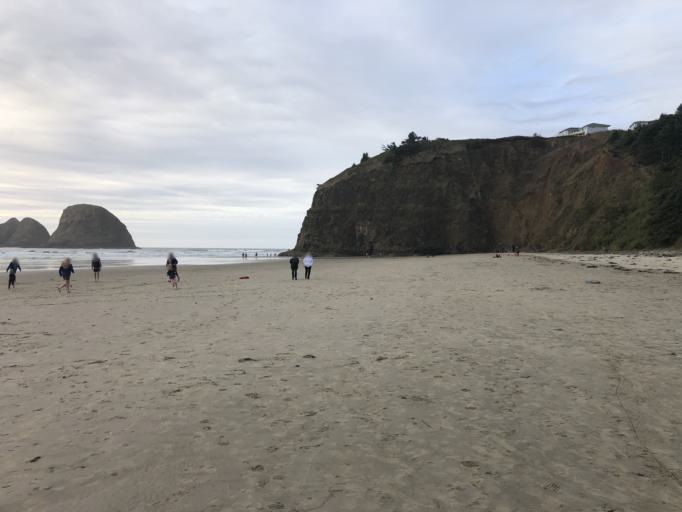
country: US
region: Oregon
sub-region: Tillamook County
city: Bay City
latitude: 45.4604
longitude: -123.9709
